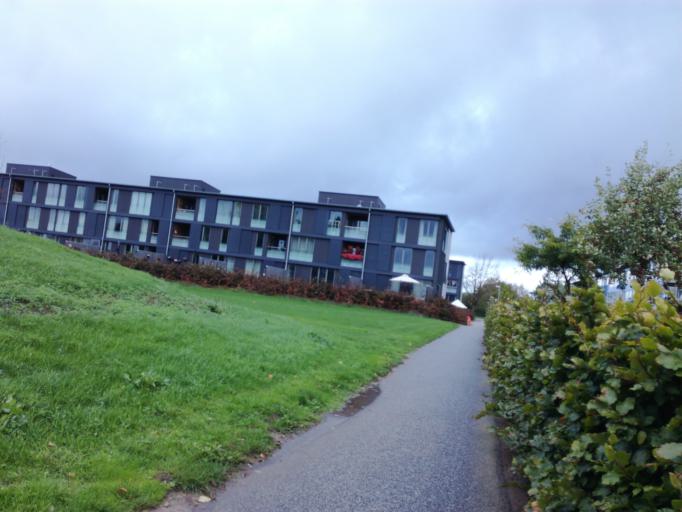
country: DK
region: South Denmark
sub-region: Fredericia Kommune
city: Fredericia
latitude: 55.5723
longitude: 9.7196
